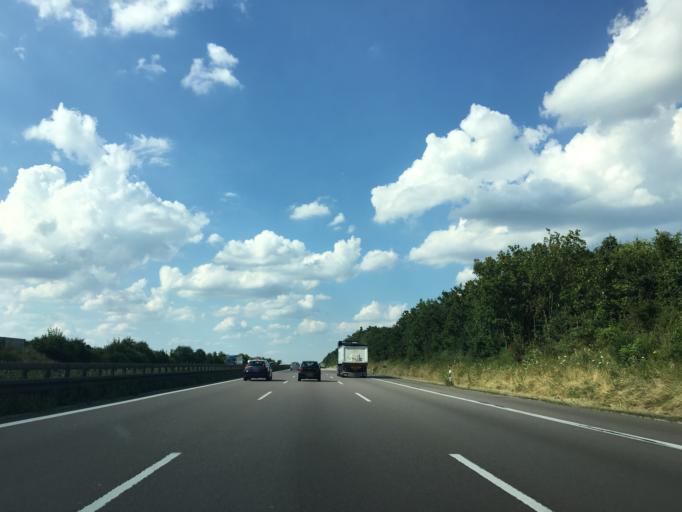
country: DE
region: Bavaria
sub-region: Regierungsbezirk Mittelfranken
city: Allersberg
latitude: 49.2646
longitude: 11.2129
